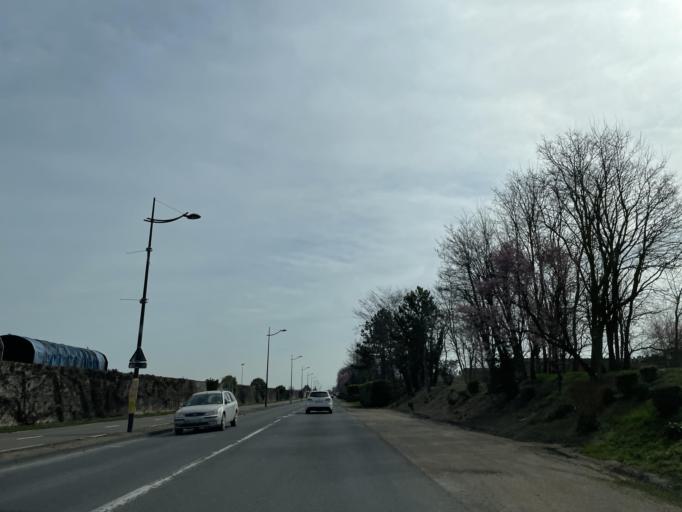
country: FR
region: Champagne-Ardenne
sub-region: Departement de l'Aube
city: Romilly-sur-Seine
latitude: 48.5091
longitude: 3.7338
